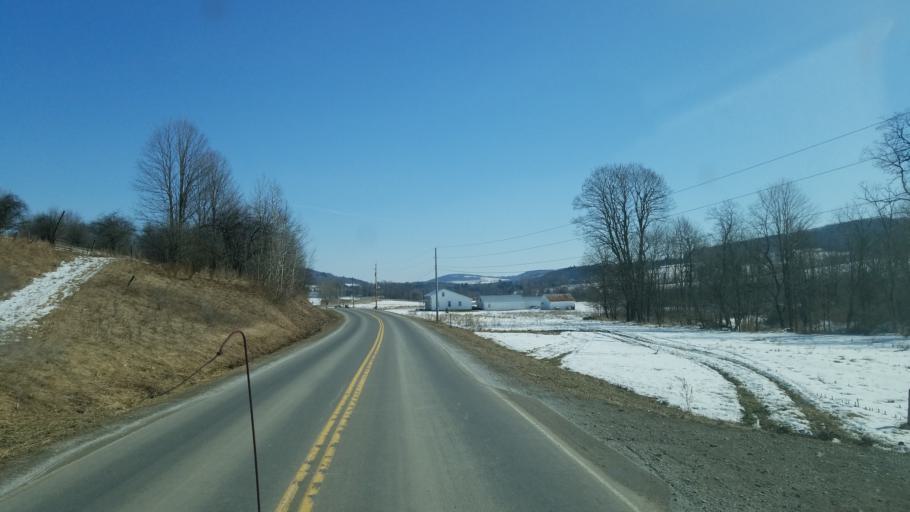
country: US
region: Pennsylvania
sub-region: Tioga County
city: Elkland
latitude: 42.0757
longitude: -77.4270
